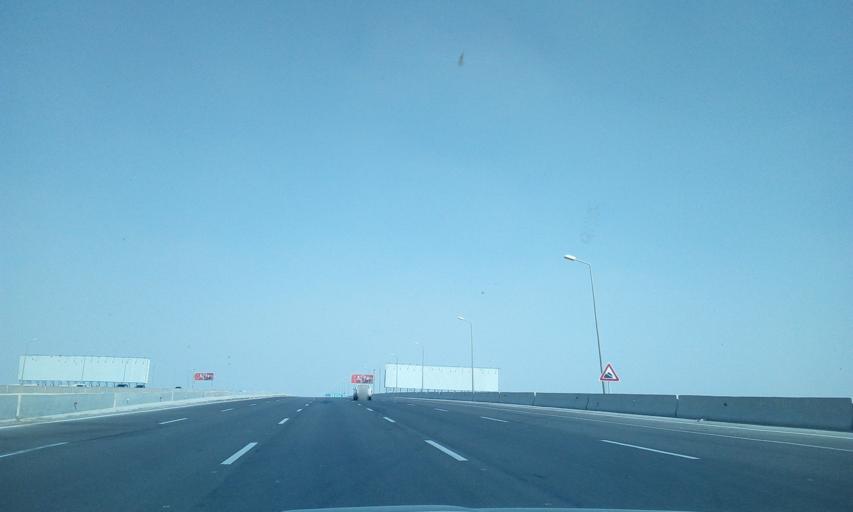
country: EG
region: As Suways
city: Ain Sukhna
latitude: 29.6932
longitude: 32.1380
